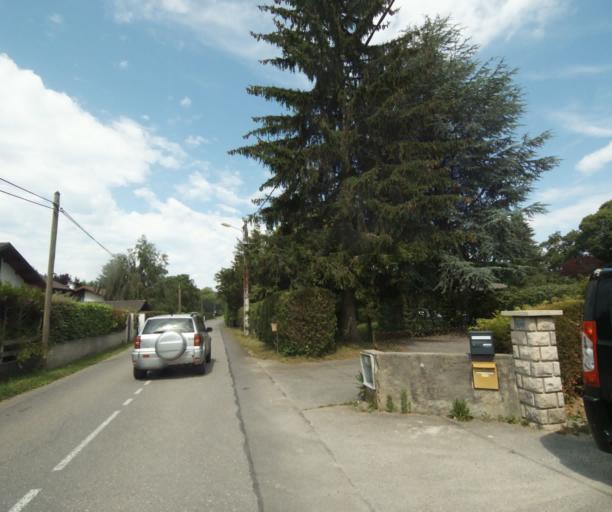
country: FR
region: Rhone-Alpes
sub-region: Departement de la Haute-Savoie
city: Armoy
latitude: 46.3477
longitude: 6.4991
